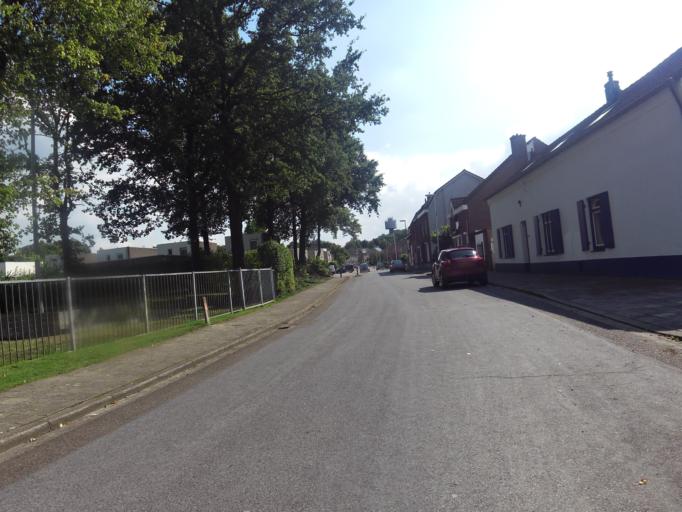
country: NL
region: Limburg
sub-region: Gemeente Brunssum
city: Brunssum
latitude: 50.9235
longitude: 5.9584
